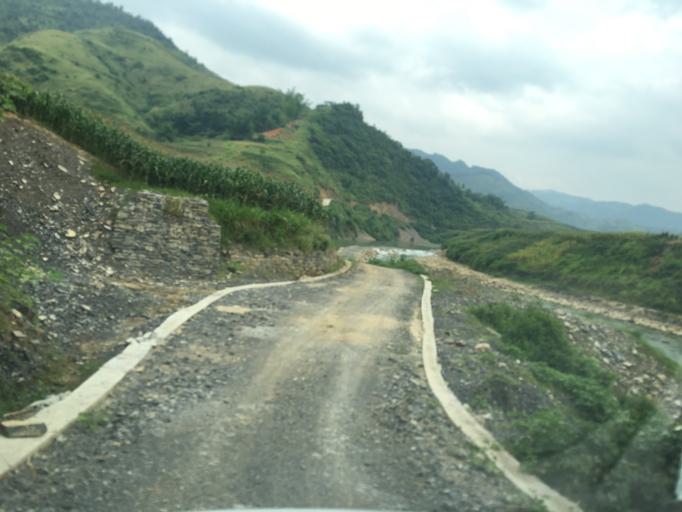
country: CN
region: Guangxi Zhuangzu Zizhiqu
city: Xinzhou
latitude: 25.1896
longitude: 105.7319
